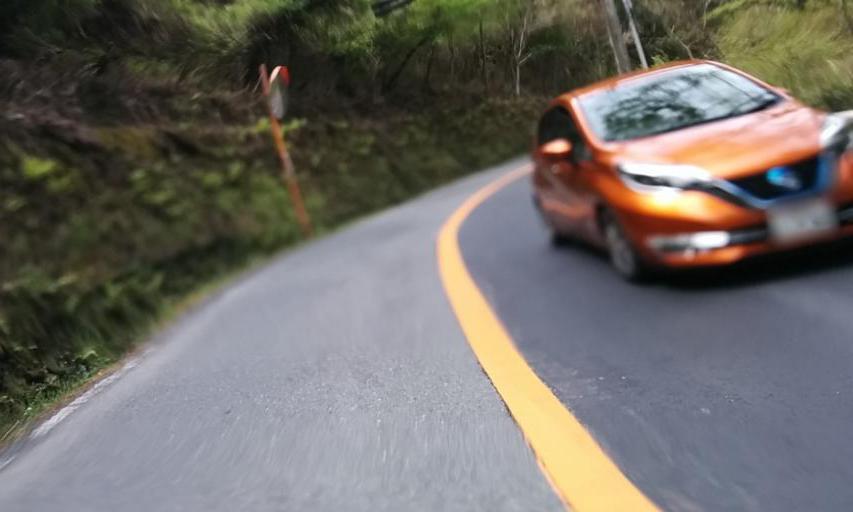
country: JP
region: Kyoto
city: Kameoka
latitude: 34.9377
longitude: 135.6004
